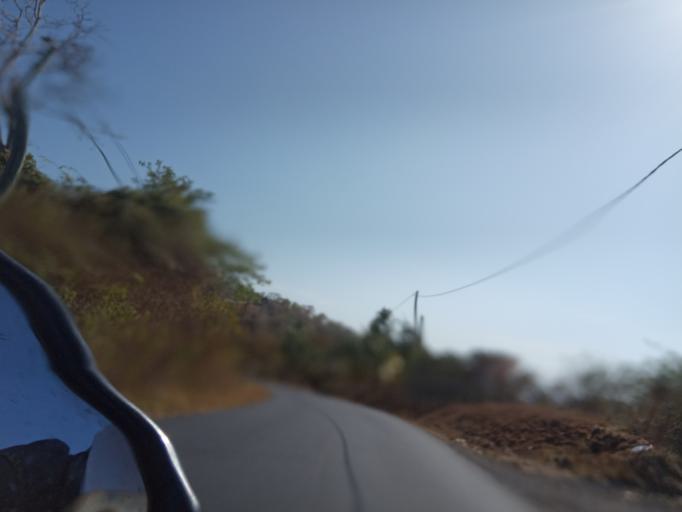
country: YT
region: Bandrele
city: Bandrele
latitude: -12.8905
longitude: 45.2099
